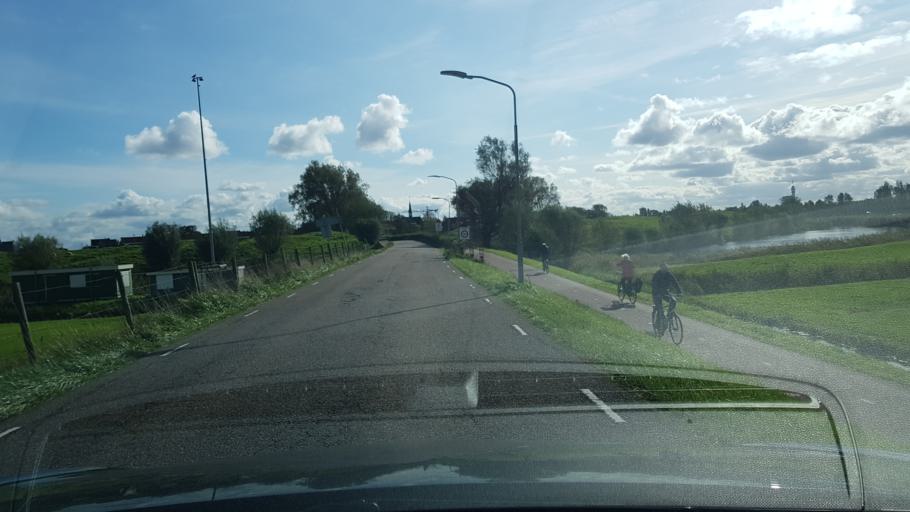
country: NL
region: North Holland
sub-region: Gemeente Velsen
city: Velsen-Zuid
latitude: 52.4180
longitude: 4.6745
